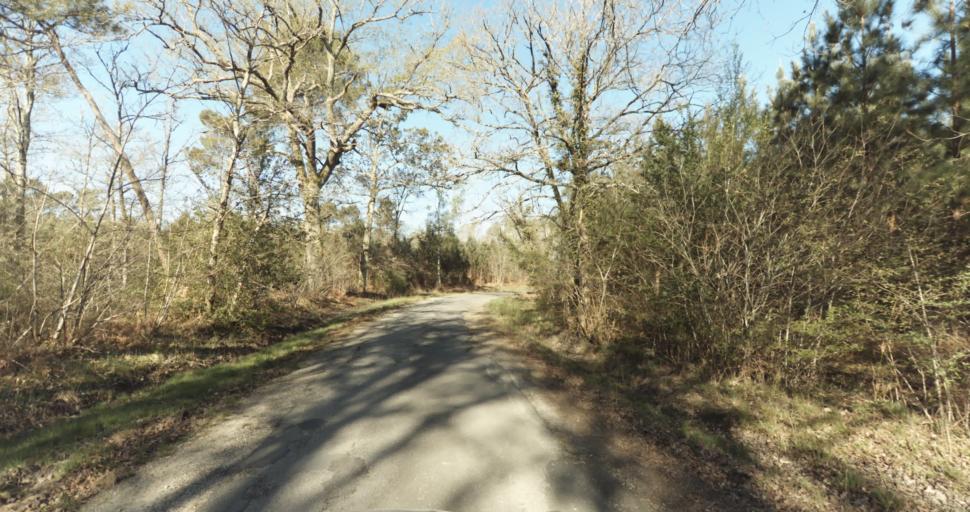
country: FR
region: Aquitaine
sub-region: Departement de la Gironde
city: Martignas-sur-Jalle
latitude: 44.8059
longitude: -0.8448
